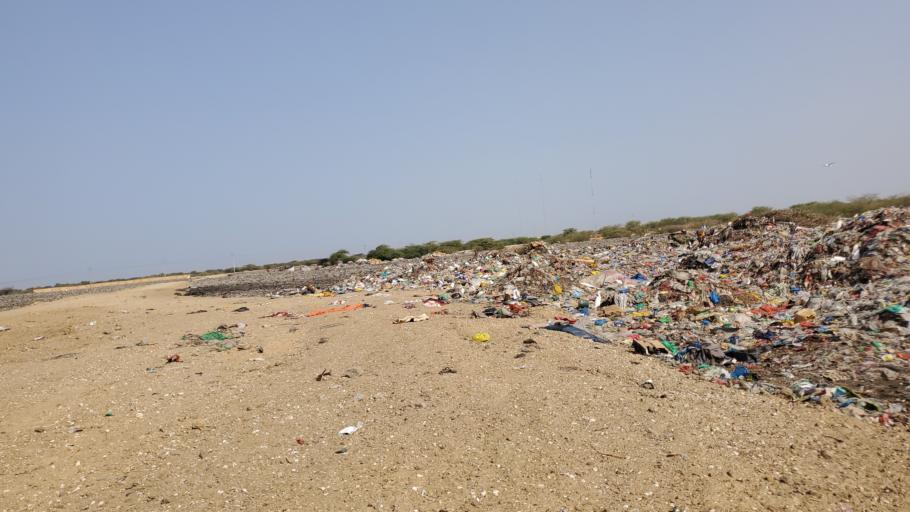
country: SN
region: Saint-Louis
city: Saint-Louis
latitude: 15.9488
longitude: -16.4304
